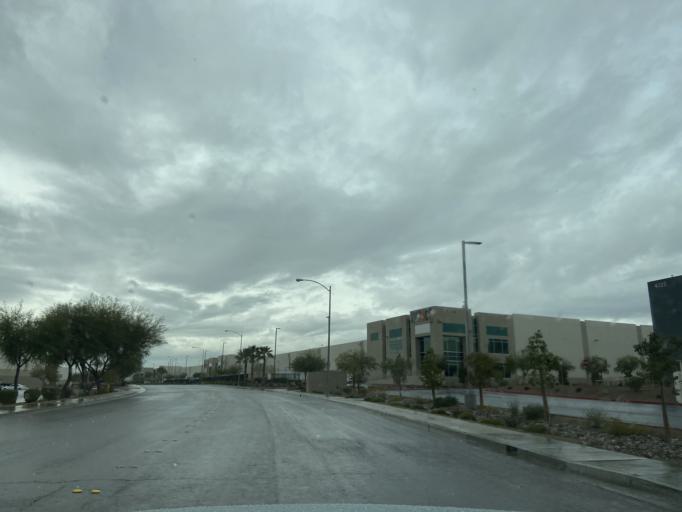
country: US
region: Nevada
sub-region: Clark County
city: Sunrise Manor
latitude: 36.2378
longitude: -115.1012
